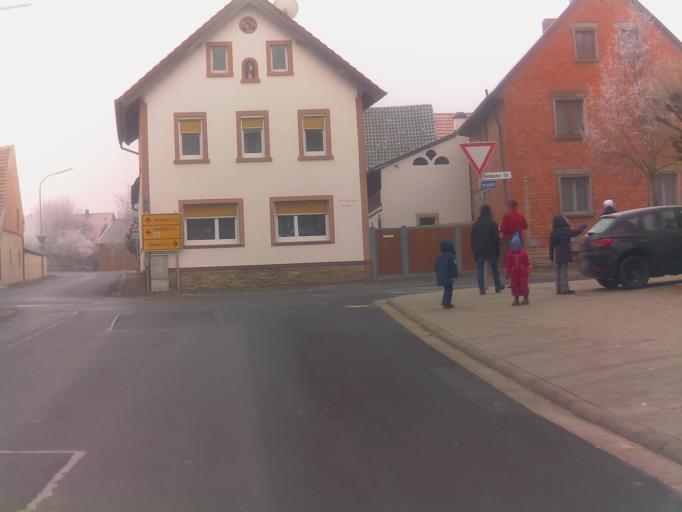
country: DE
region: Bavaria
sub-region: Regierungsbezirk Unterfranken
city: Lulsfeld
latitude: 49.8680
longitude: 10.3200
